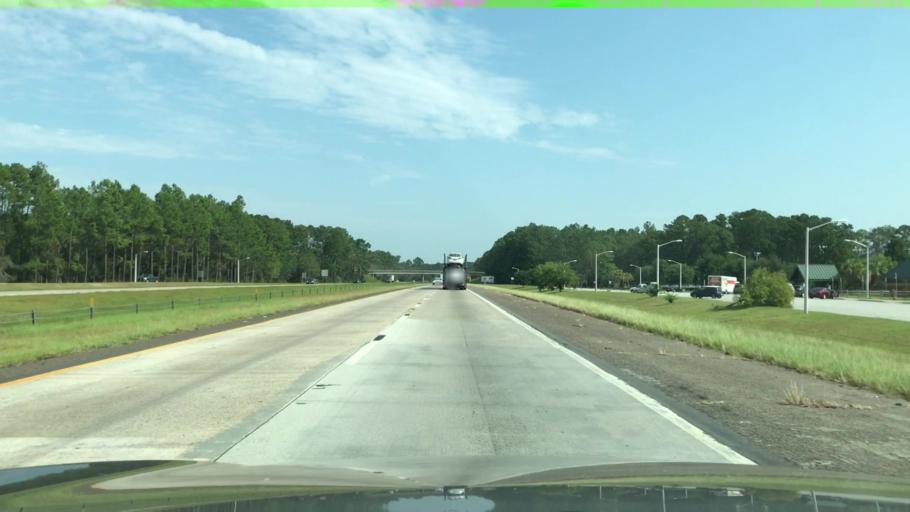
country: US
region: South Carolina
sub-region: Hampton County
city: Yemassee
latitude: 32.8009
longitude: -80.7714
